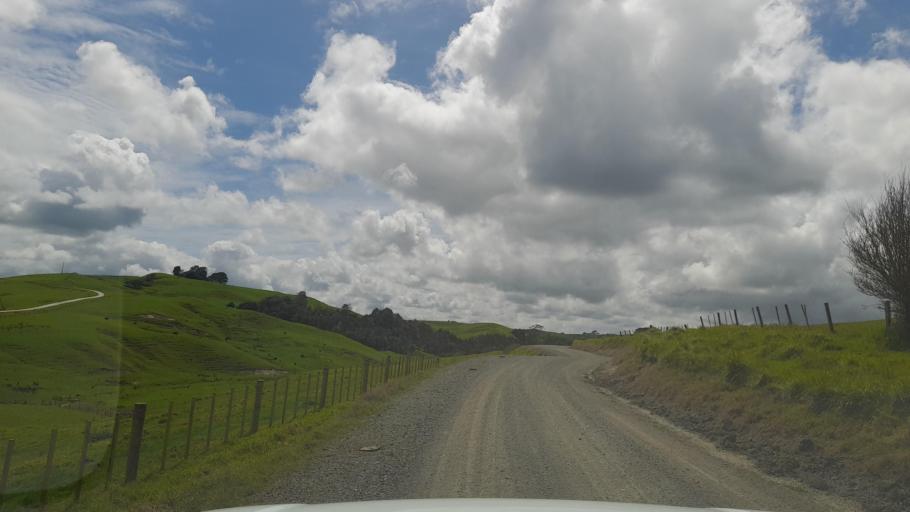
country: NZ
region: Auckland
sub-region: Auckland
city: Wellsford
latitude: -36.2140
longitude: 174.3235
